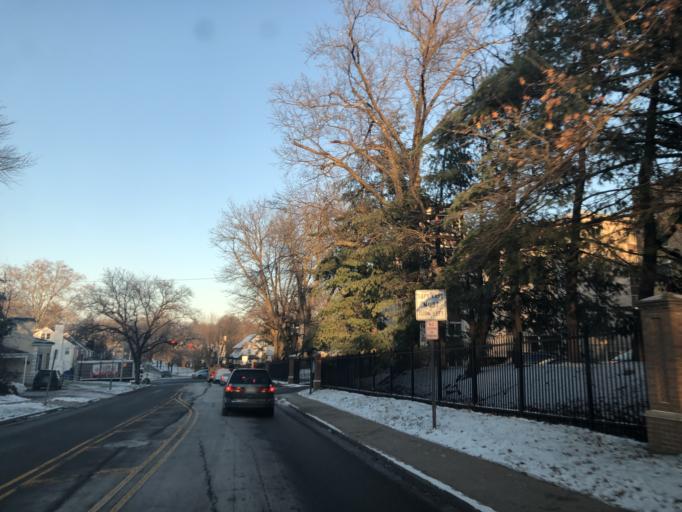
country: US
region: New Jersey
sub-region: Essex County
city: South Orange
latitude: 40.7438
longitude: -74.2492
